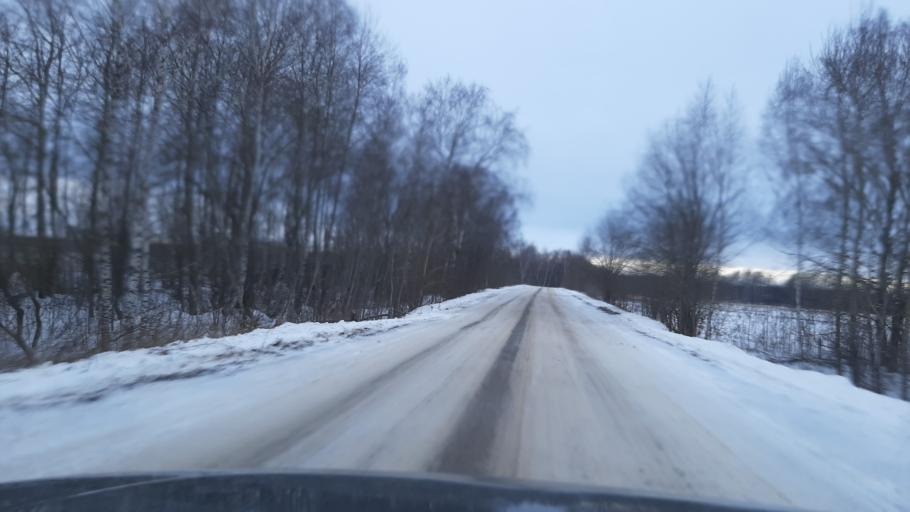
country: RU
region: Kostroma
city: Volgorechensk
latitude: 57.4373
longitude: 41.0511
